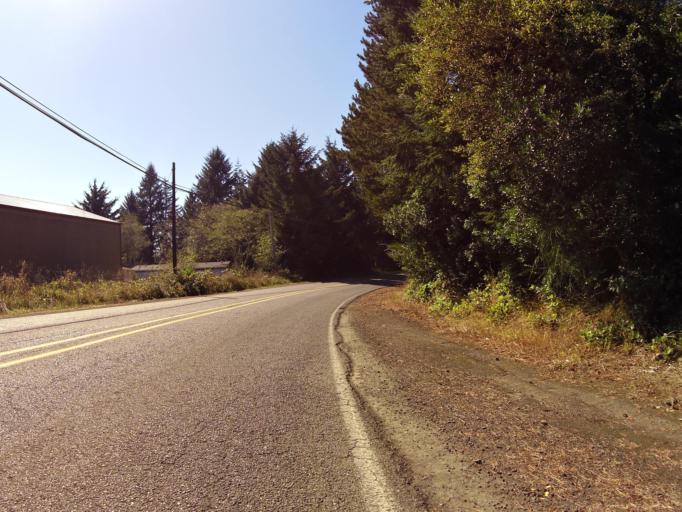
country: US
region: Oregon
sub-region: Coos County
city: Barview
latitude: 43.3304
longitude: -124.3378
